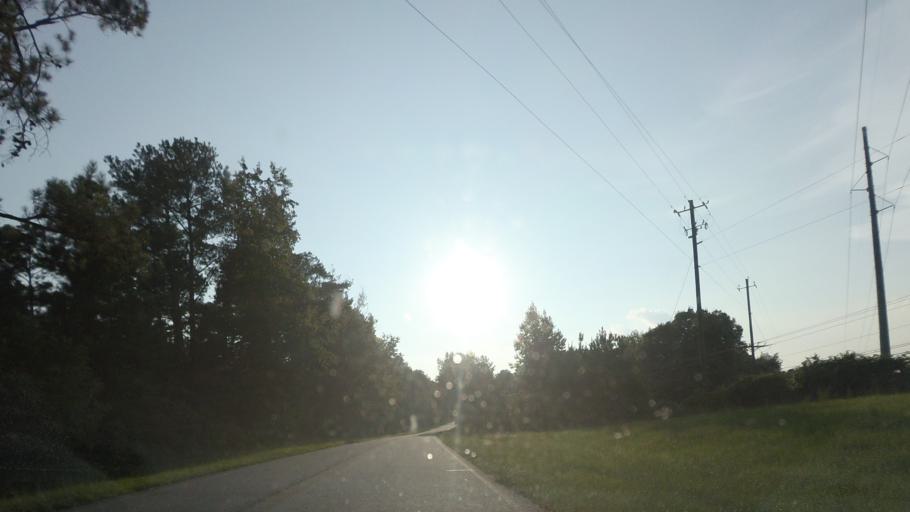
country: US
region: Georgia
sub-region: Bibb County
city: West Point
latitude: 32.9408
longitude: -83.7580
